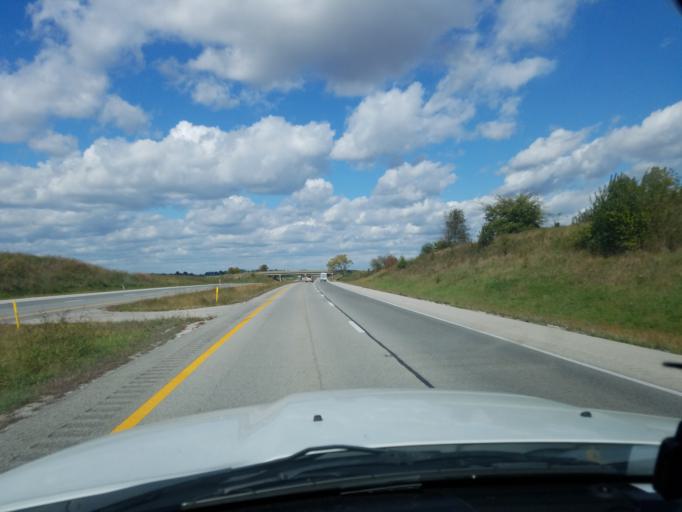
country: US
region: Kentucky
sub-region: Daviess County
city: Masonville
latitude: 37.6740
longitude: -87.0270
